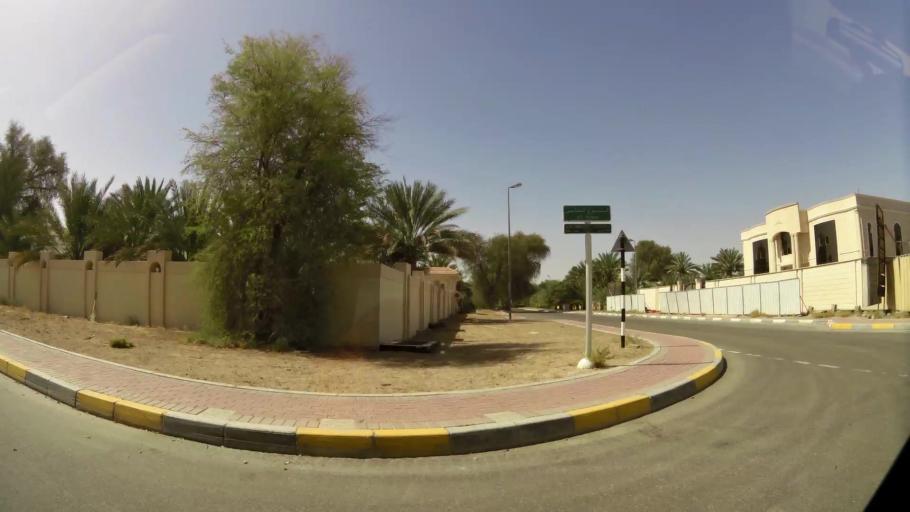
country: OM
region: Al Buraimi
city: Al Buraymi
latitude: 24.2983
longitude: 55.7752
